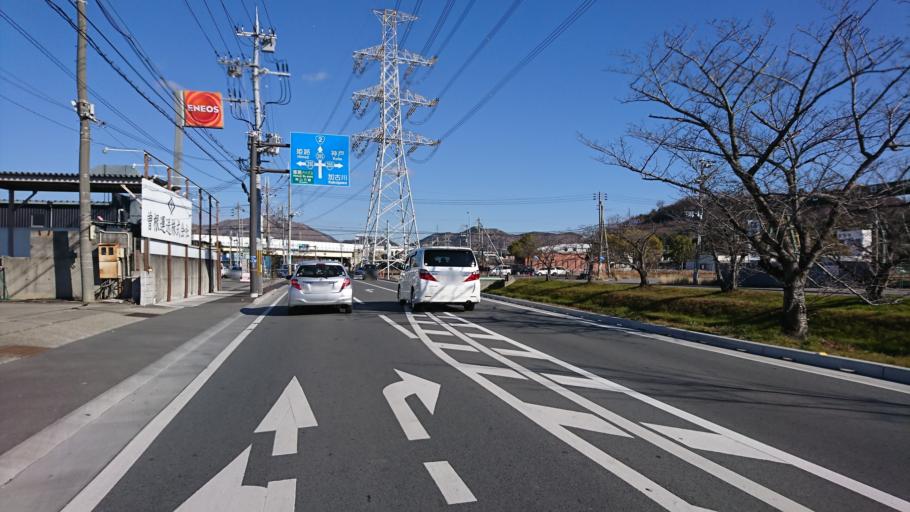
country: JP
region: Hyogo
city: Kakogawacho-honmachi
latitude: 34.7840
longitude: 134.7821
